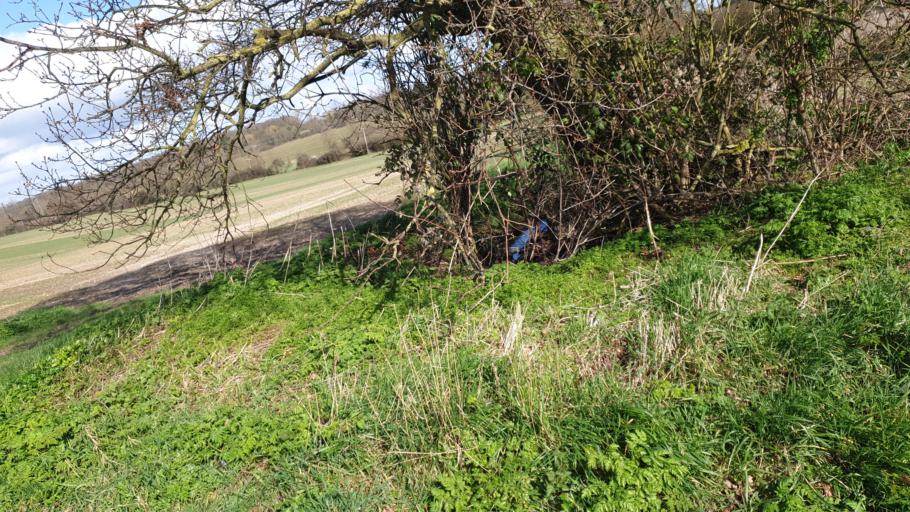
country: GB
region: England
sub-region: Essex
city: Little Clacton
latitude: 51.8400
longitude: 1.1661
